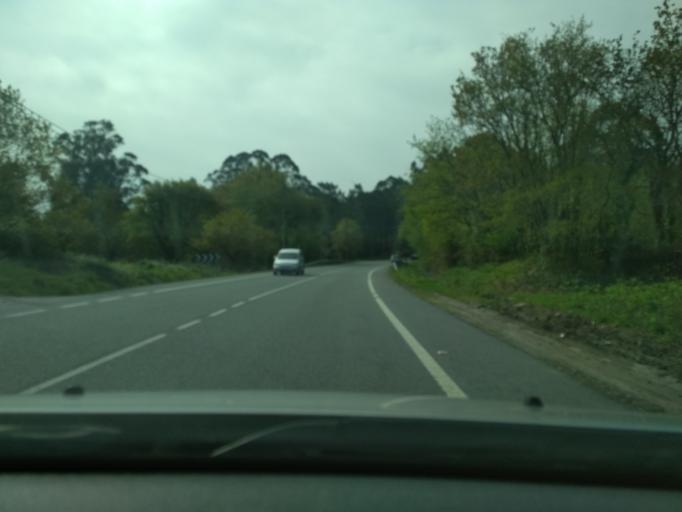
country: ES
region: Galicia
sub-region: Provincia de Pontevedra
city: Catoira
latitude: 42.6679
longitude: -8.7044
